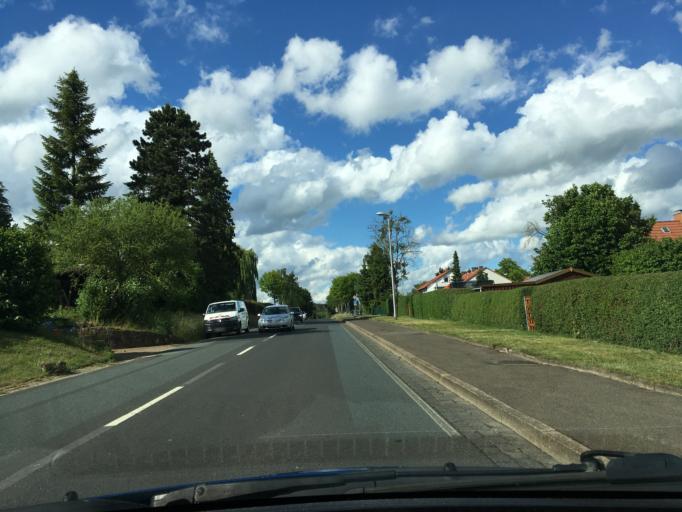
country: DE
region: Lower Saxony
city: Moringen
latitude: 51.7066
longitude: 9.8736
